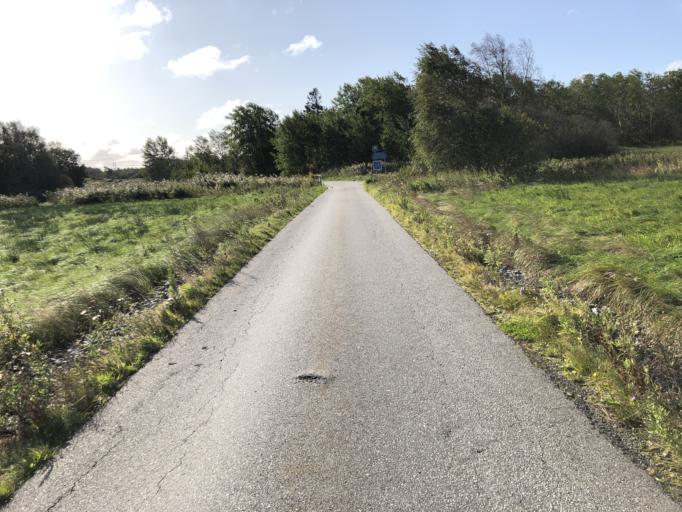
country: SE
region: Vaestra Goetaland
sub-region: Goteborg
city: Torslanda
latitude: 57.7409
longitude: 11.8189
